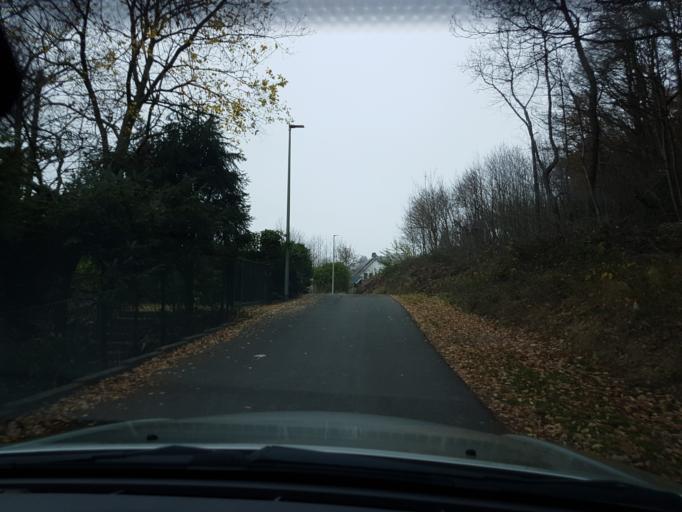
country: DE
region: Hesse
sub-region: Regierungsbezirk Darmstadt
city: Schlangenbad
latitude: 50.1137
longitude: 8.0992
